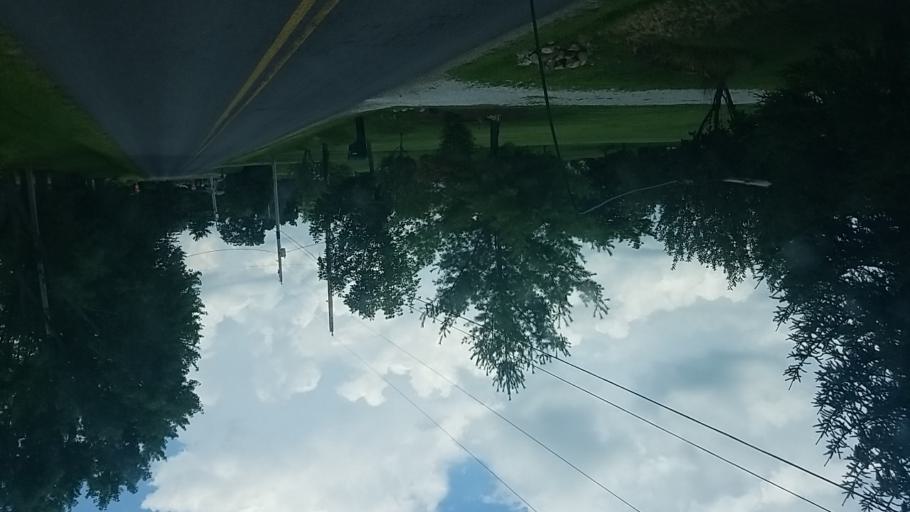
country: US
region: Ohio
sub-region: Medina County
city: Lodi
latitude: 41.0843
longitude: -82.0759
